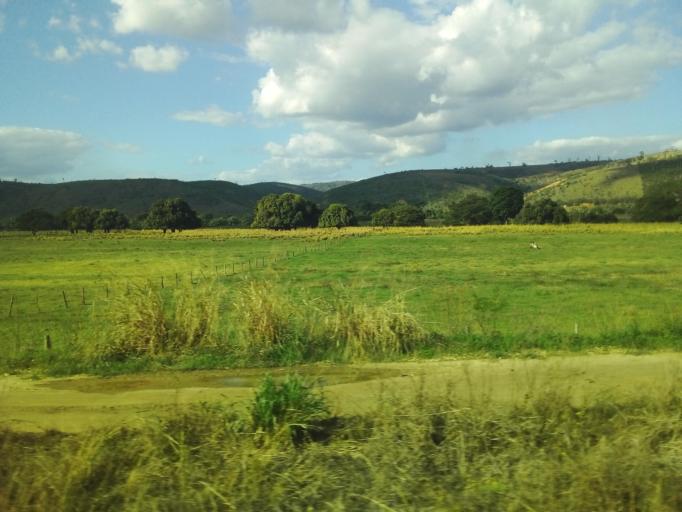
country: BR
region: Minas Gerais
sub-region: Conselheiro Pena
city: Conselheiro Pena
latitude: -19.1204
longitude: -41.5012
